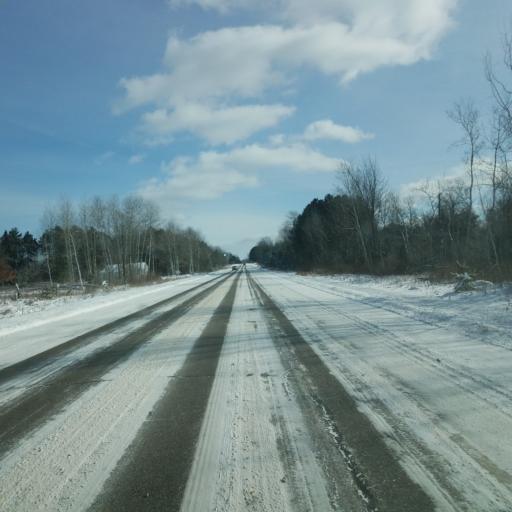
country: US
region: Michigan
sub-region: Osceola County
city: Evart
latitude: 43.9008
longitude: -85.1333
